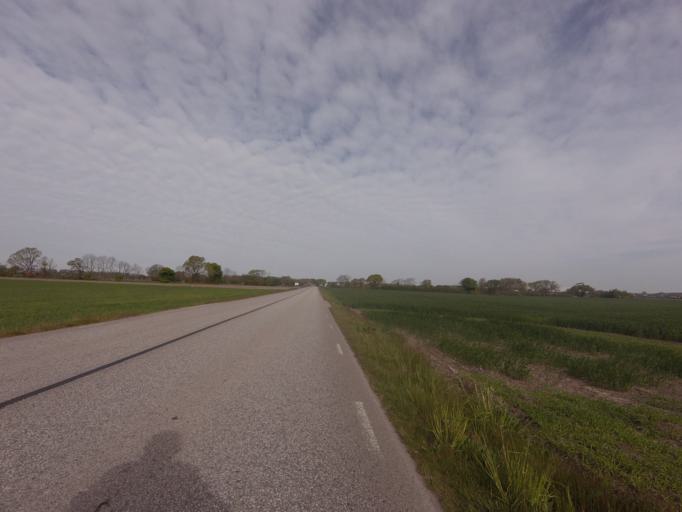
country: SE
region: Skane
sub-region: Hoganas Kommun
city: Hoganas
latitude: 56.1862
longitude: 12.5906
